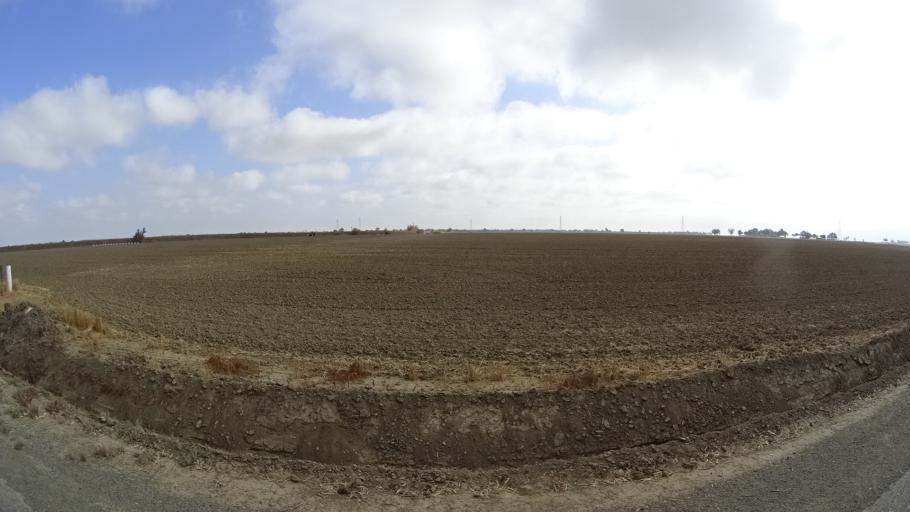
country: US
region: California
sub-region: Yolo County
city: Woodland
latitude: 38.8004
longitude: -121.7744
